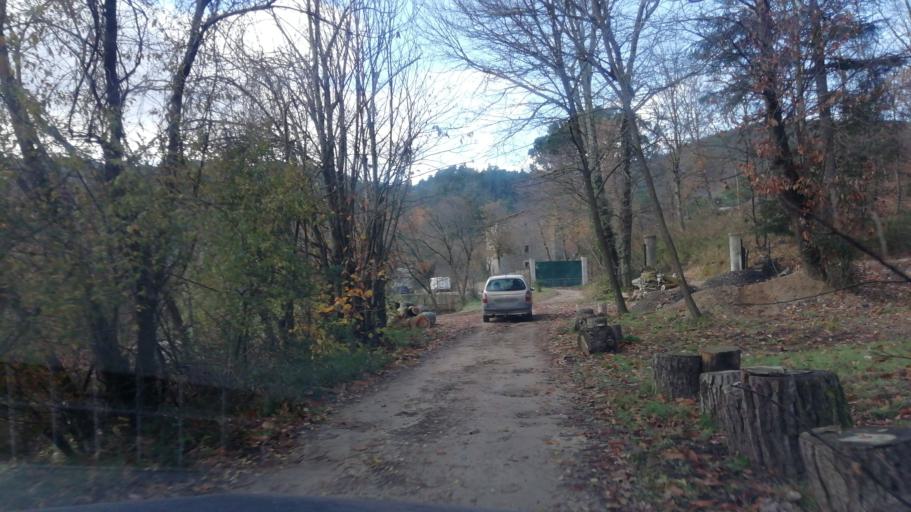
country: FR
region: Languedoc-Roussillon
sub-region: Departement du Gard
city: Lasalle
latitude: 44.0314
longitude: 3.8570
